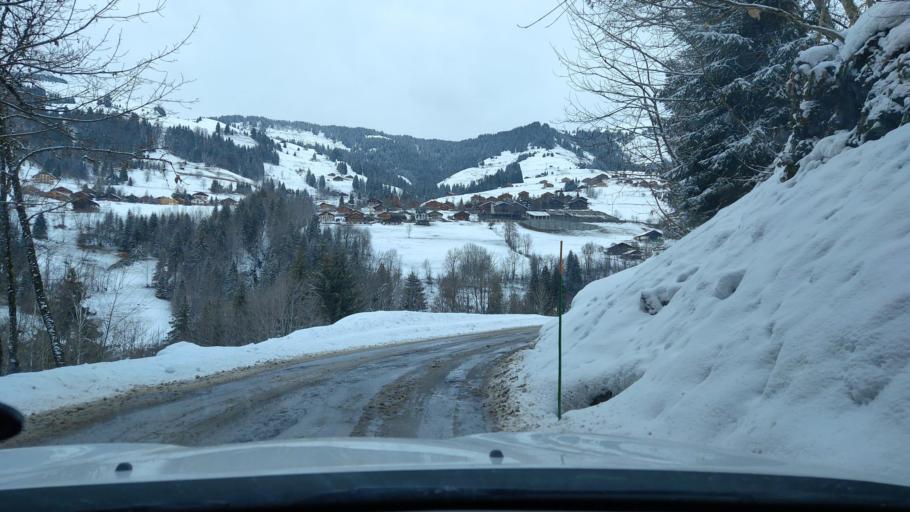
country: FR
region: Rhone-Alpes
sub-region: Departement de la Savoie
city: Beaufort
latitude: 45.7431
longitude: 6.5850
